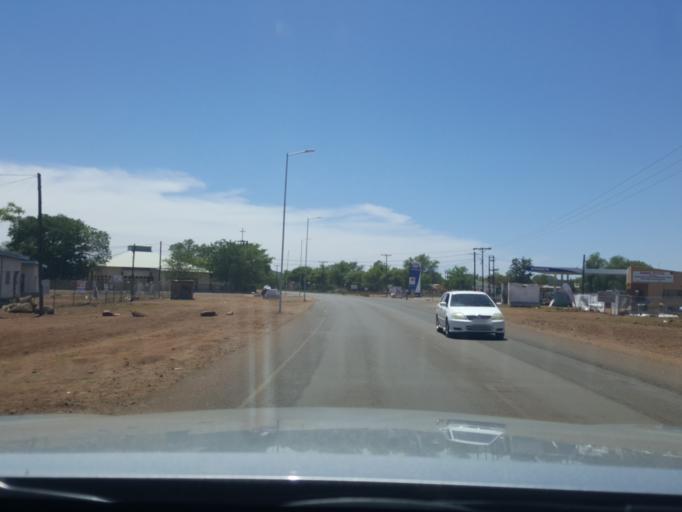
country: BW
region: South East
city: Ramotswa
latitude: -24.8679
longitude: 25.8702
